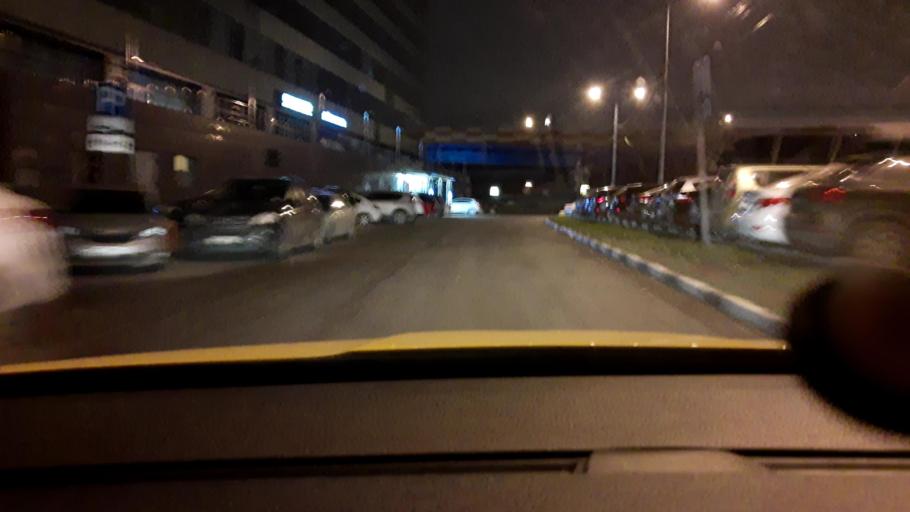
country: RU
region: Moskovskaya
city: Pavshino
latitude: 55.8146
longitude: 37.3538
